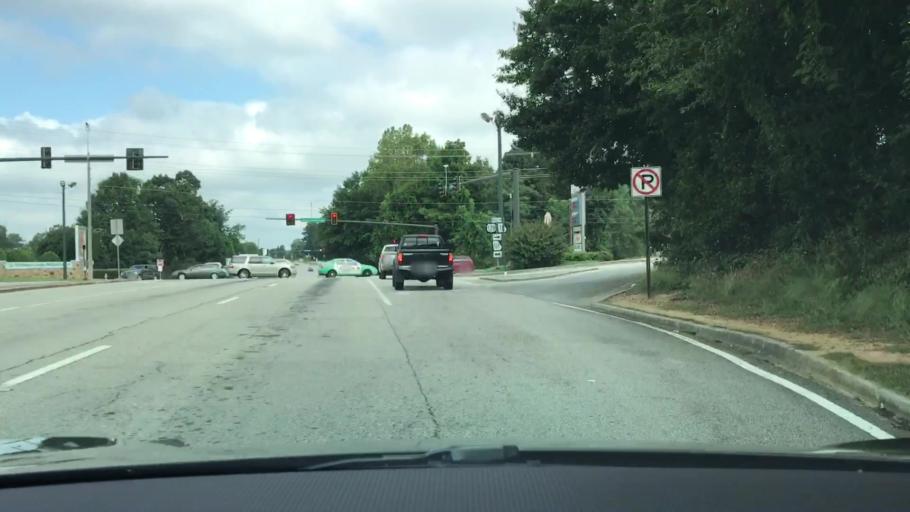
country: US
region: Georgia
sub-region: Hall County
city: Gainesville
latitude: 34.3025
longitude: -83.8124
